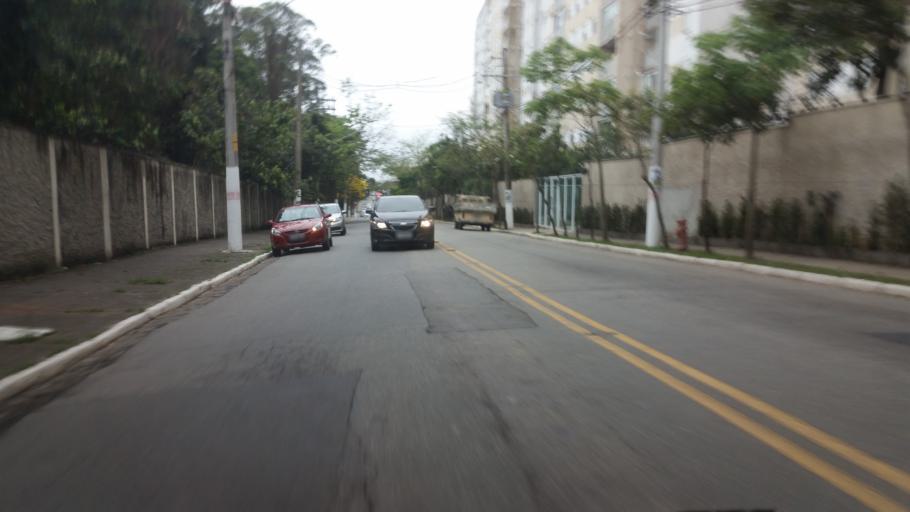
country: BR
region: Sao Paulo
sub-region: Diadema
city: Diadema
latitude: -23.6576
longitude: -46.6155
